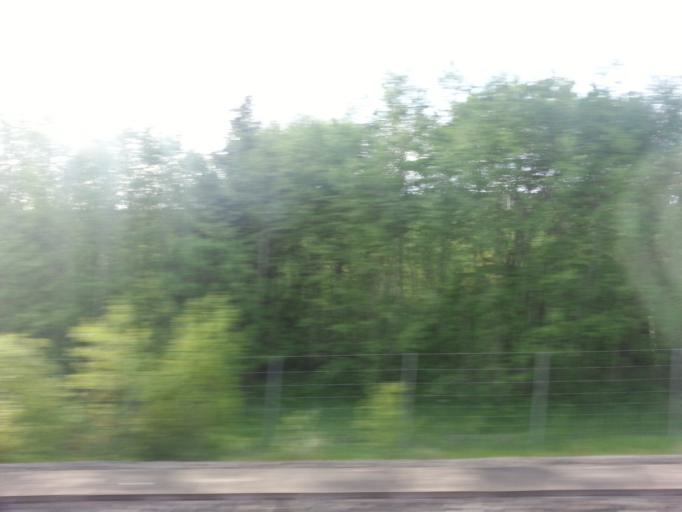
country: NO
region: Akershus
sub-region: Sorum
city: Frogner
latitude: 60.0094
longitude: 11.1018
